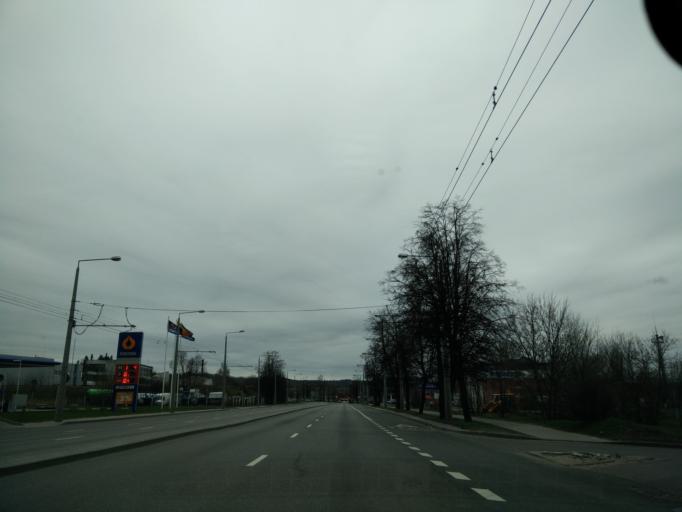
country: LT
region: Vilnius County
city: Vilkpede
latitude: 54.6624
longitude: 25.2350
